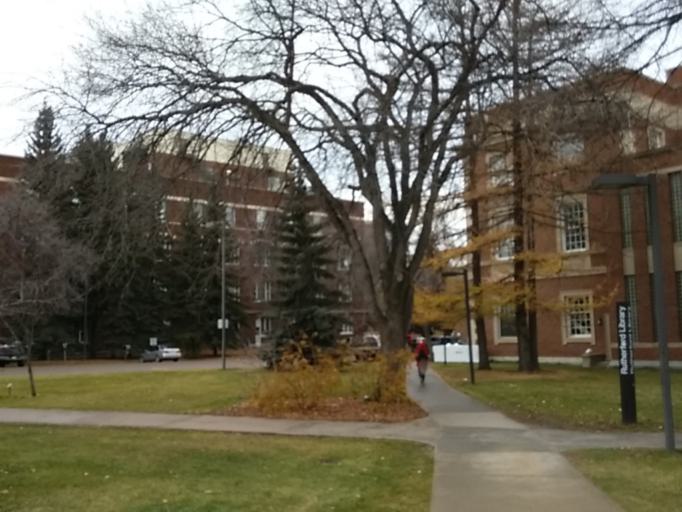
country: CA
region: Alberta
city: Edmonton
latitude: 53.5251
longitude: -113.5216
